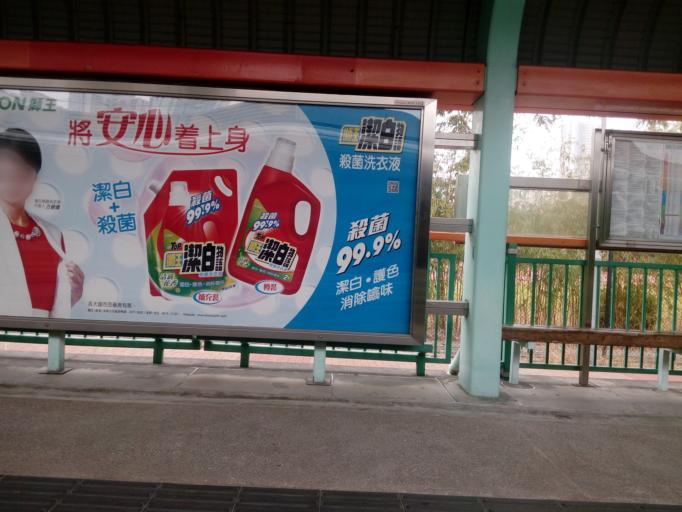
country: HK
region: Yuen Long
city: Yuen Long Kau Hui
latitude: 22.4549
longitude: 114.0056
